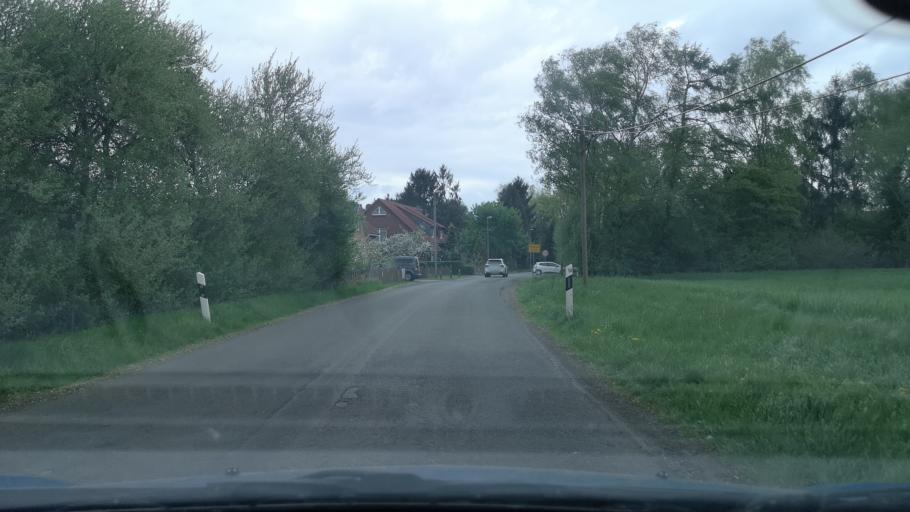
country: DE
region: Lower Saxony
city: Langenhagen
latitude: 52.4868
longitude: 9.7392
